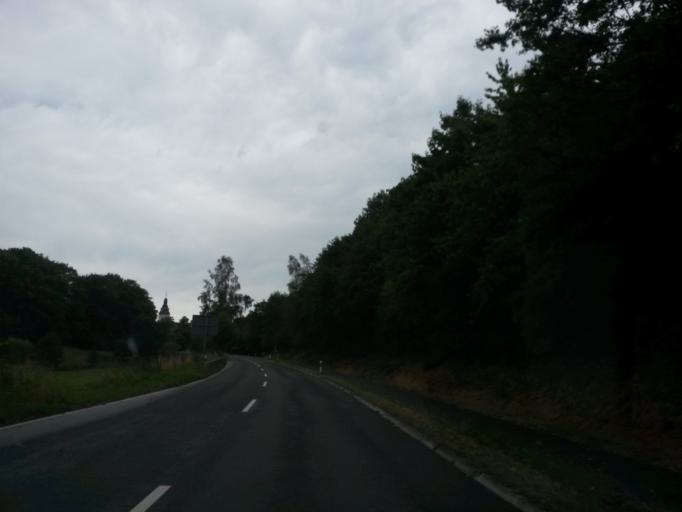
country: DE
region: North Rhine-Westphalia
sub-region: Regierungsbezirk Koln
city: Numbrecht
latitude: 50.8976
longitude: 7.5393
